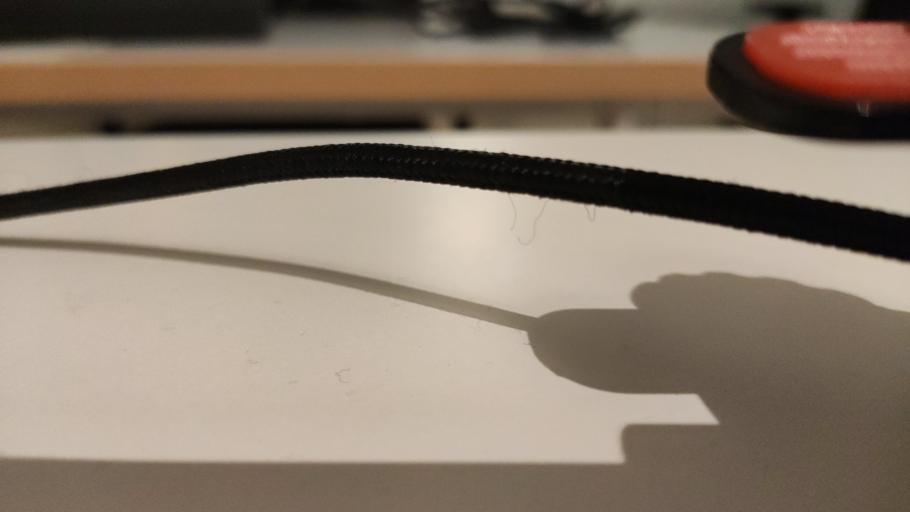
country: RU
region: Moskovskaya
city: Rogachevo
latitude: 56.4393
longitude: 37.1789
